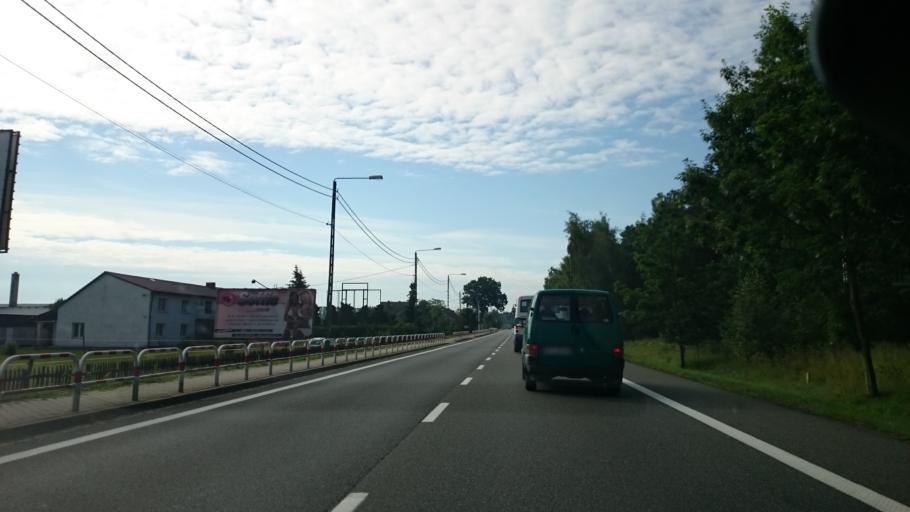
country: PL
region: Opole Voivodeship
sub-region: Powiat opolski
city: Tarnow Opolski
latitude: 50.6101
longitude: 18.0701
